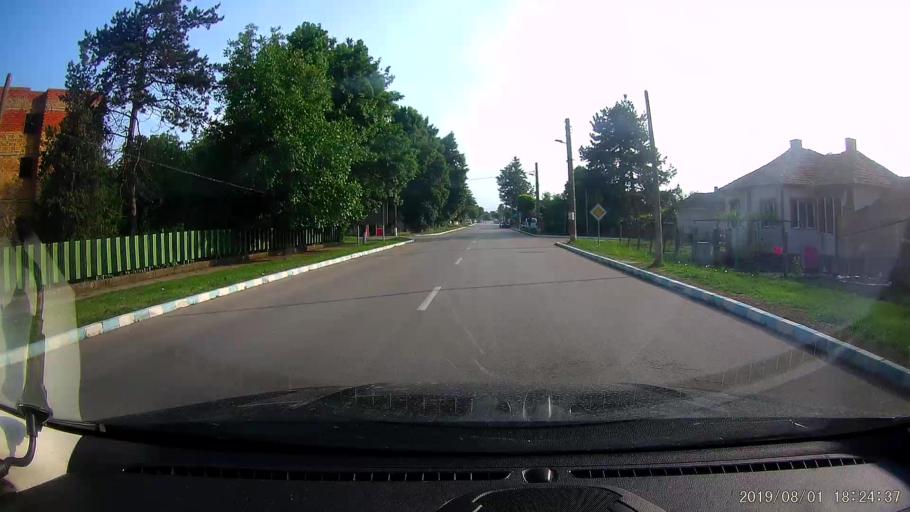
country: BG
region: Shumen
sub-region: Obshtina Venets
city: Venets
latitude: 43.6237
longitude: 27.0048
